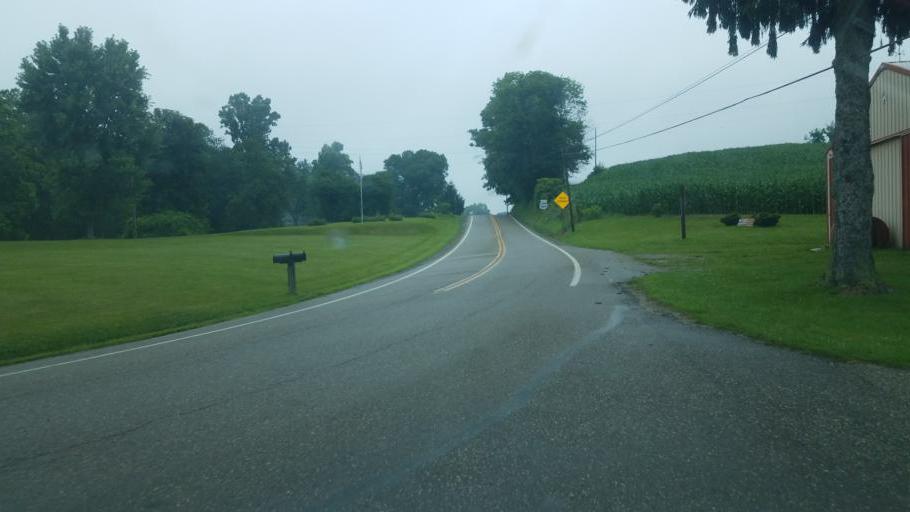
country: US
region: Ohio
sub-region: Carroll County
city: Carrollton
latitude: 40.4571
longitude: -81.0992
